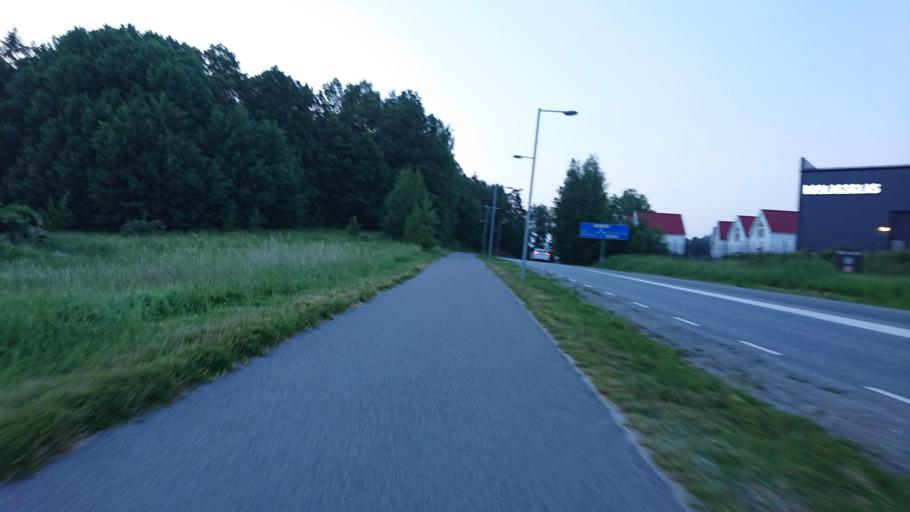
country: SE
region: Stockholm
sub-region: Osterakers Kommun
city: Akersberga
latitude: 59.4846
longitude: 18.2729
